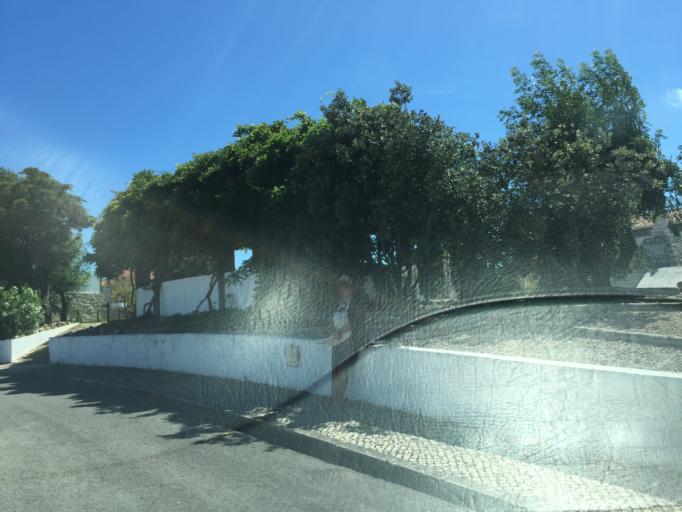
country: PT
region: Lisbon
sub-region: Torres Vedras
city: A dos Cunhados
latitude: 39.1765
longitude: -9.3156
